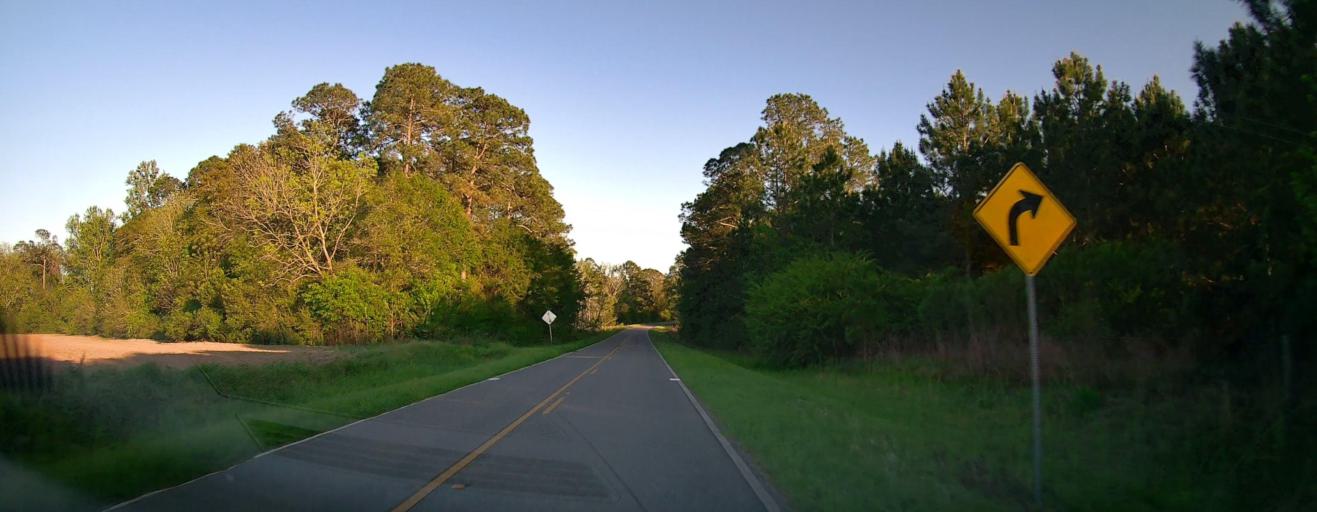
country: US
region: Georgia
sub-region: Ben Hill County
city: Fitzgerald
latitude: 31.6916
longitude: -83.2336
